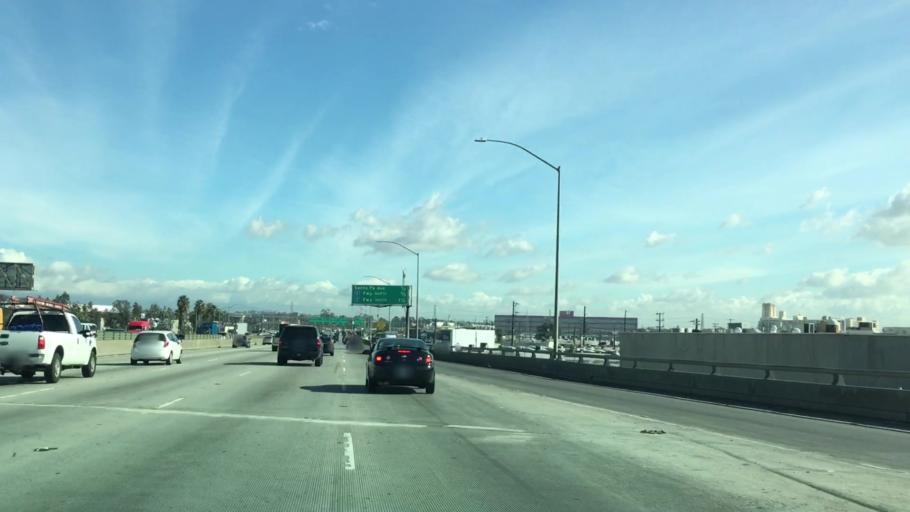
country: US
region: California
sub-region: Los Angeles County
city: Los Angeles
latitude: 34.0245
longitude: -118.2395
